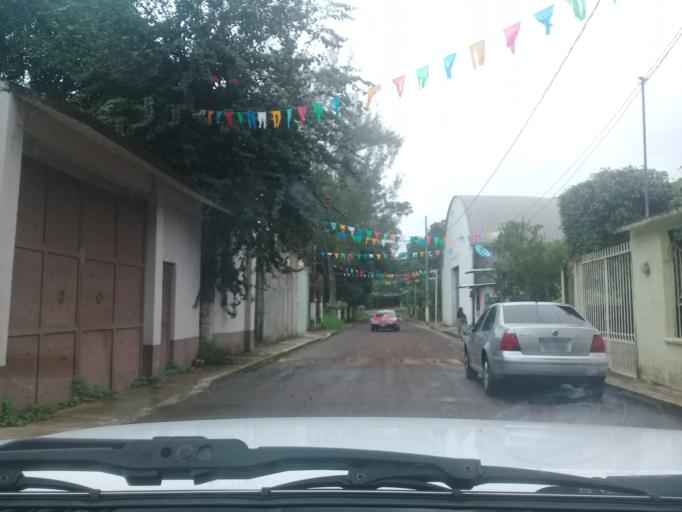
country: MX
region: Veracruz
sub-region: San Andres Tuxtla
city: Cerro las Iguanas
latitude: 18.4300
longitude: -95.1979
